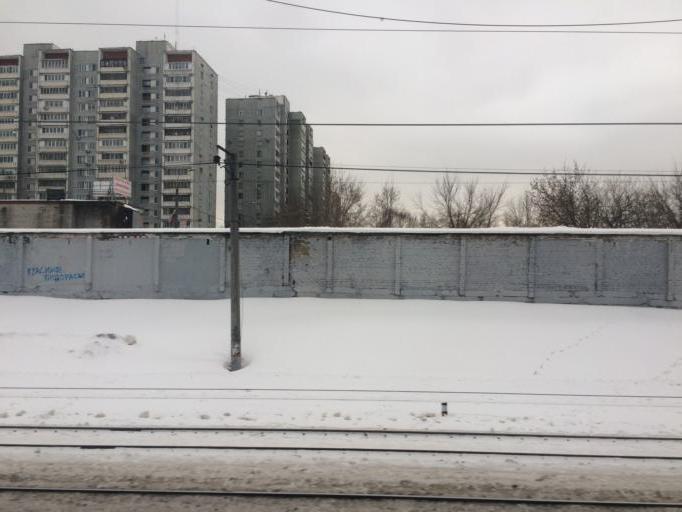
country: RU
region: Moscow
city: Mar'ina Roshcha
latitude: 55.8009
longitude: 37.6185
